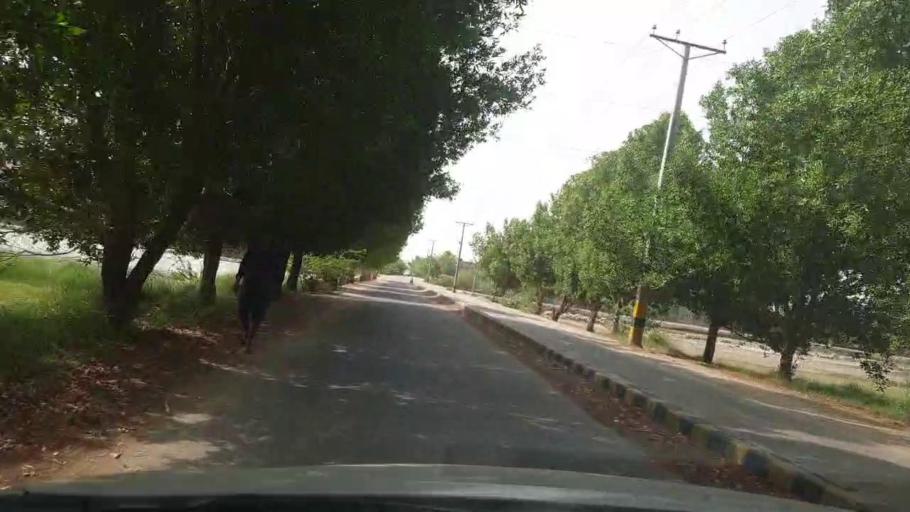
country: PK
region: Sindh
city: Kot Diji
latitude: 27.3509
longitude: 68.7120
